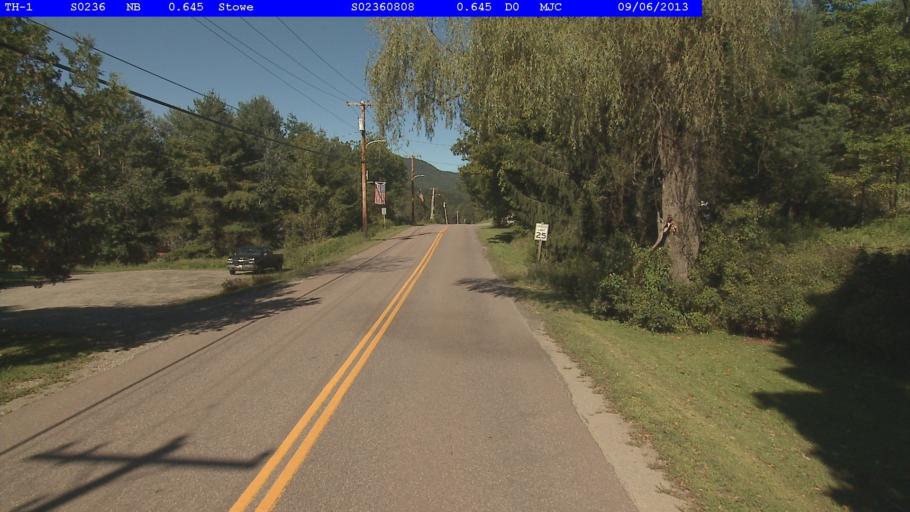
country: US
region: Vermont
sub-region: Washington County
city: Waterbury
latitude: 44.4422
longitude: -72.7187
